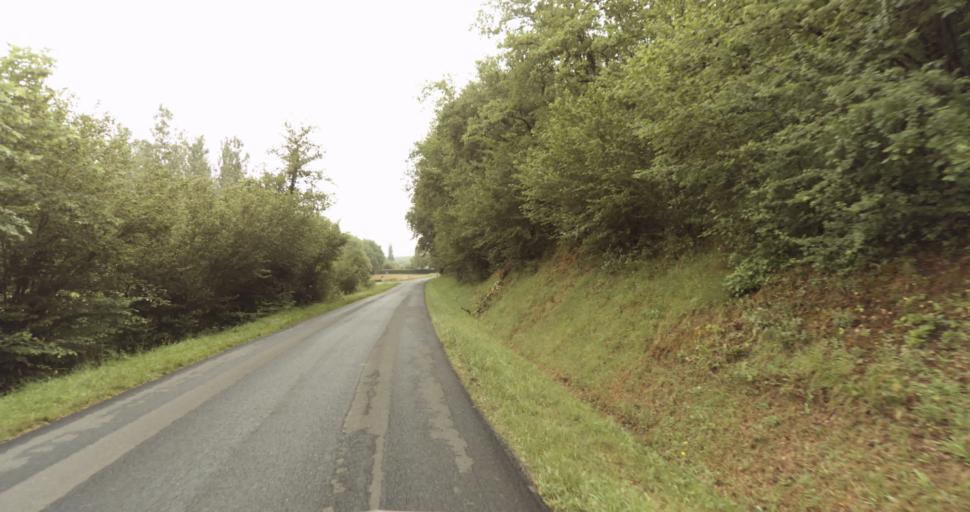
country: FR
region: Aquitaine
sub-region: Departement de la Dordogne
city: Lalinde
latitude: 44.8729
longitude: 0.7731
